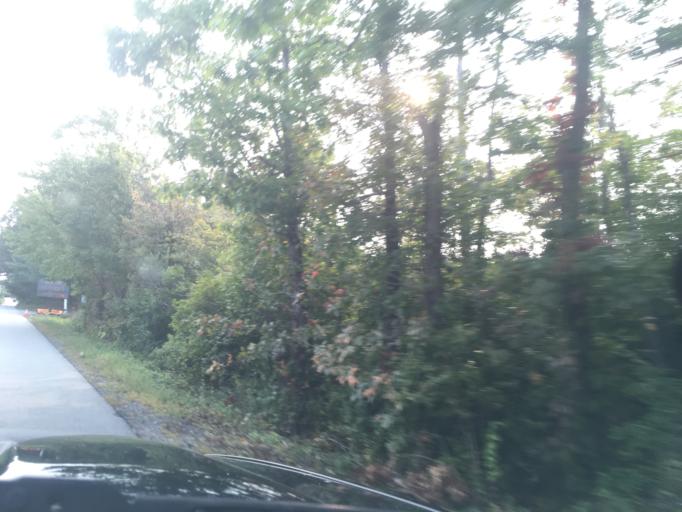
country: US
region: New Hampshire
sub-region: Rockingham County
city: Stratham Station
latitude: 43.0030
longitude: -70.8818
